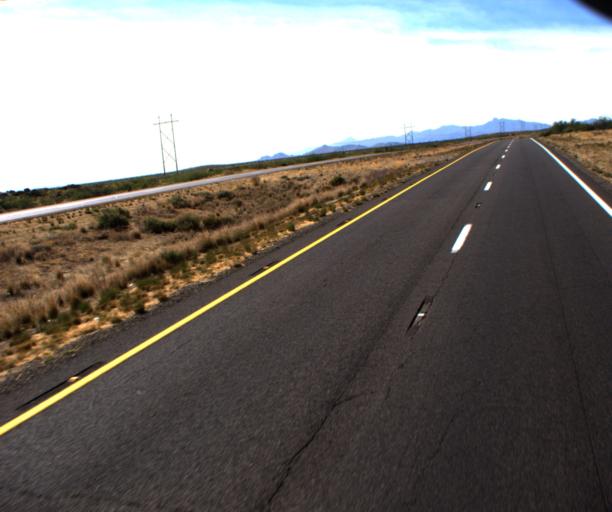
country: US
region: Arizona
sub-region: Graham County
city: Swift Trail Junction
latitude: 32.5310
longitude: -109.6747
